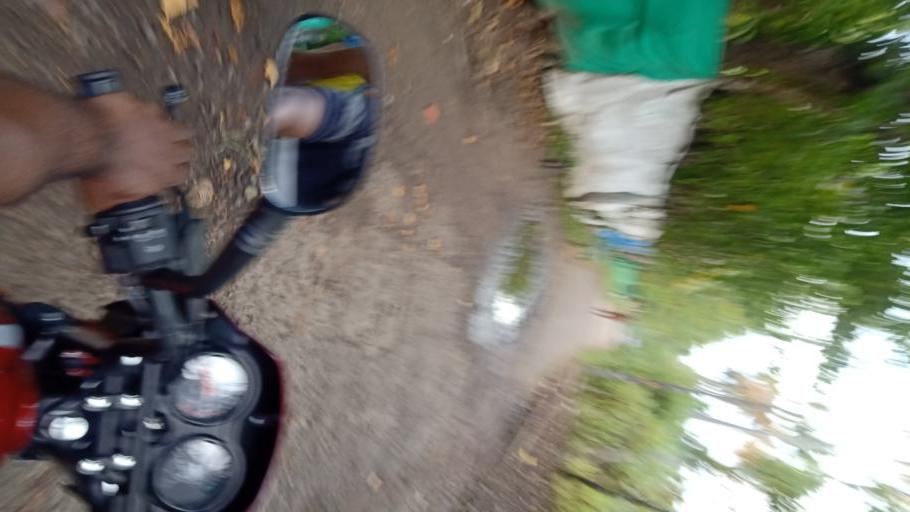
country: IN
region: Kerala
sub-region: Ernakulam
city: Elur
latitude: 10.0295
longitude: 76.2108
